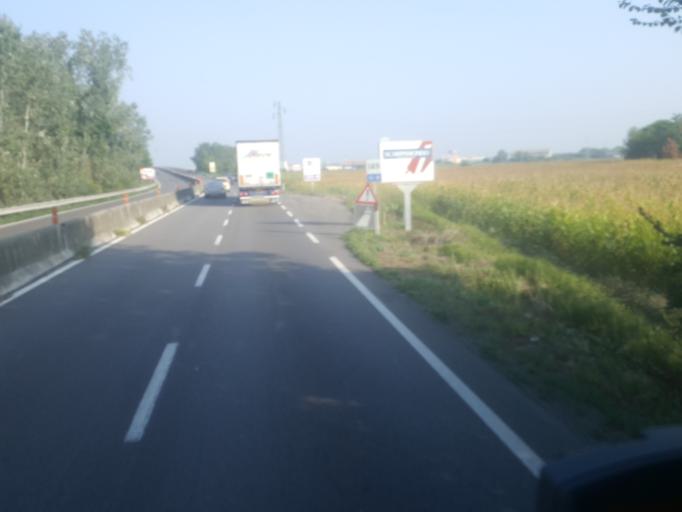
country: IT
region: Emilia-Romagna
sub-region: Provincia di Ravenna
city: Ravenna
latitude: 44.4170
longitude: 12.1683
